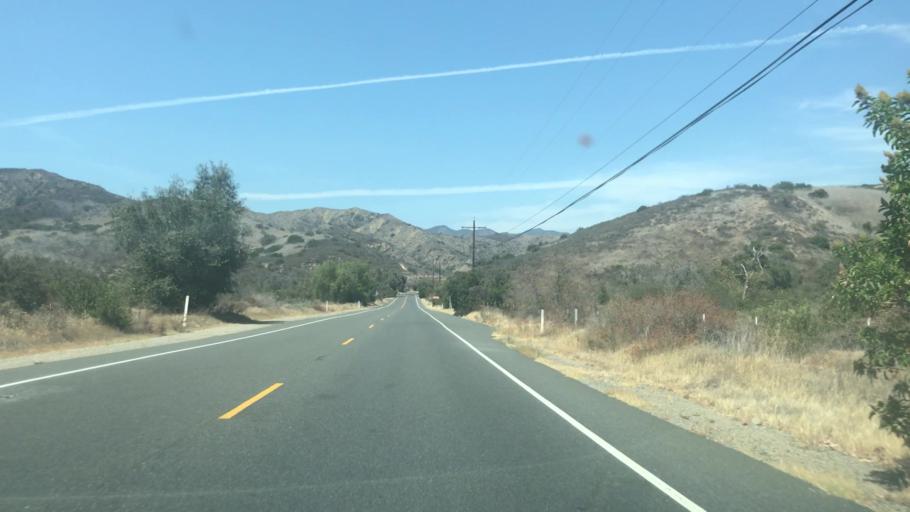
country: US
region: California
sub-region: Orange County
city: Coto De Caza
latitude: 33.5693
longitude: -117.5435
